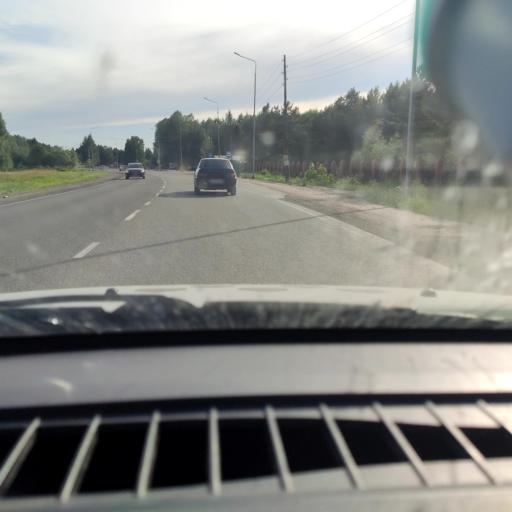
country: RU
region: Kirov
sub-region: Kirovo-Chepetskiy Rayon
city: Kirov
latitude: 58.6216
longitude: 49.7774
